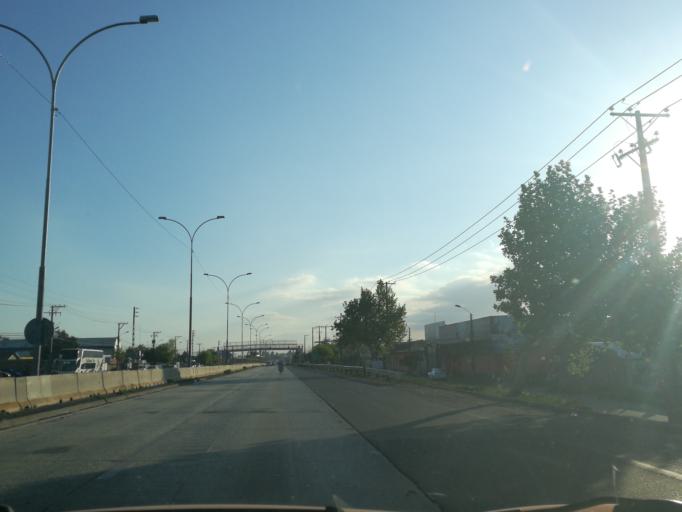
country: CL
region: O'Higgins
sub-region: Provincia de Cachapoal
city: Rancagua
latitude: -34.1805
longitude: -70.7352
